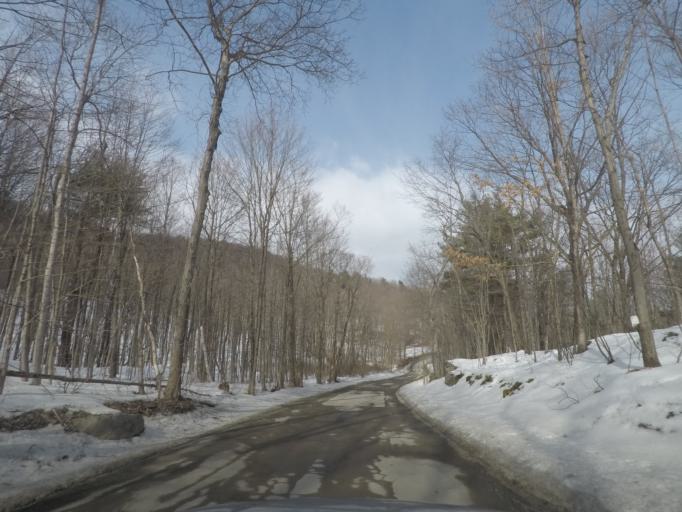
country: US
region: New York
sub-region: Saratoga County
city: Waterford
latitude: 42.7822
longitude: -73.5934
